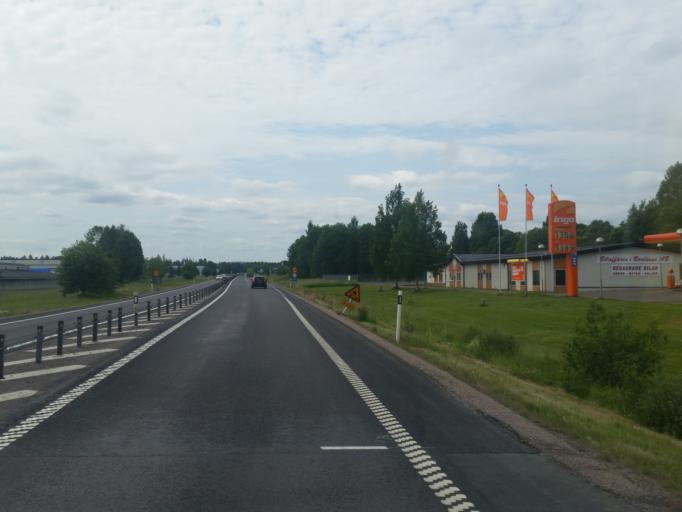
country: SE
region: Dalarna
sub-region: Borlange Kommun
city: Borlaenge
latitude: 60.4757
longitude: 15.4061
